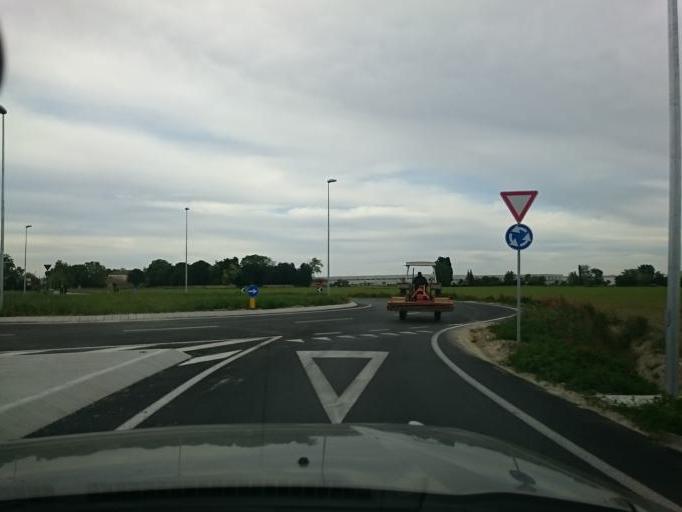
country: IT
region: Veneto
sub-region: Provincia di Padova
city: Monselice
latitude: 45.2103
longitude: 11.7346
